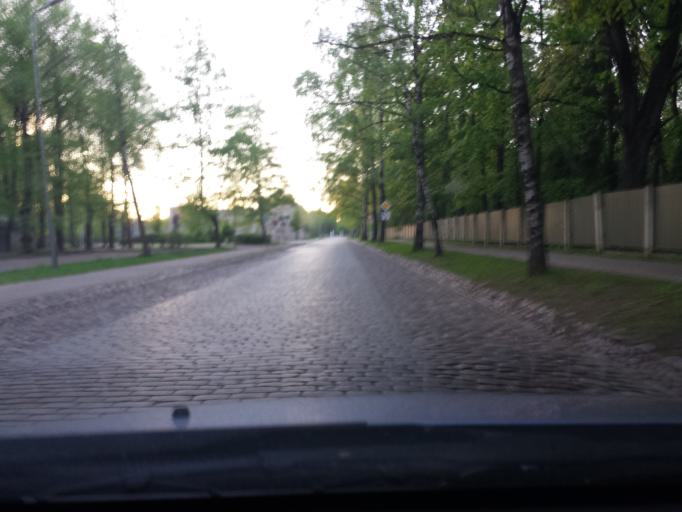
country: LV
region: Riga
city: Riga
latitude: 56.9841
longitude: 24.1483
